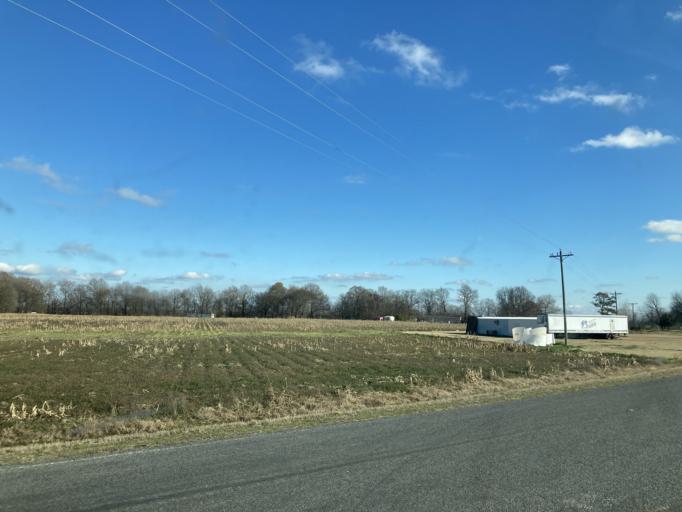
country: US
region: Mississippi
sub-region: Yazoo County
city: Yazoo City
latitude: 32.9277
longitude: -90.4715
